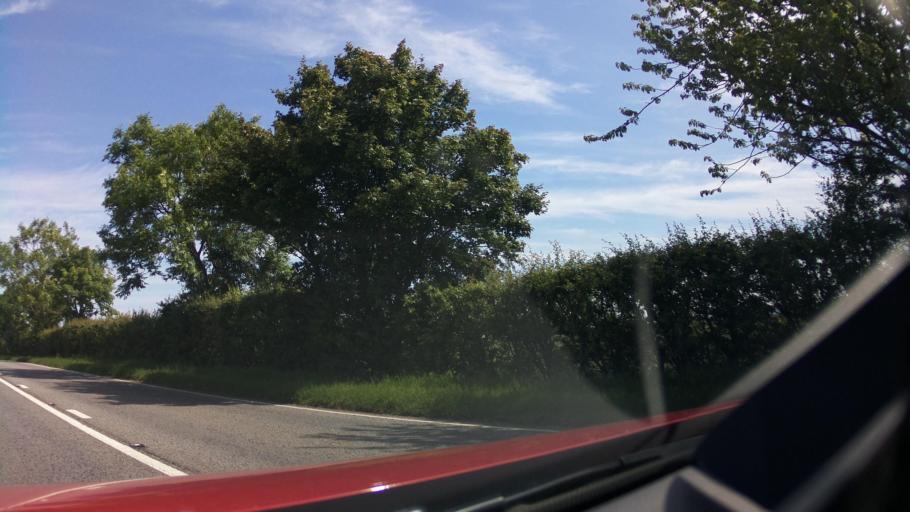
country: GB
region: England
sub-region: North Lincolnshire
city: Kirton in Lindsey
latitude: 53.3800
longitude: -0.5467
